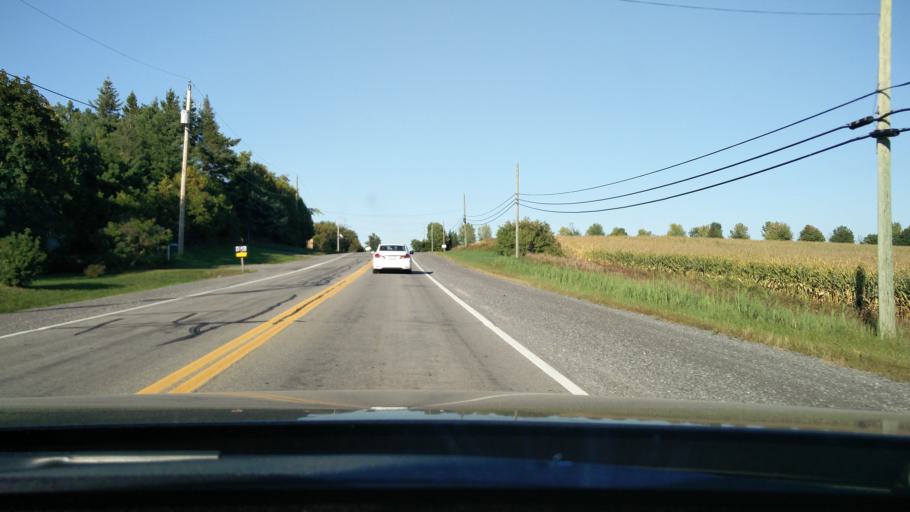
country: CA
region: Ontario
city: Bells Corners
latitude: 45.1464
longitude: -75.9144
